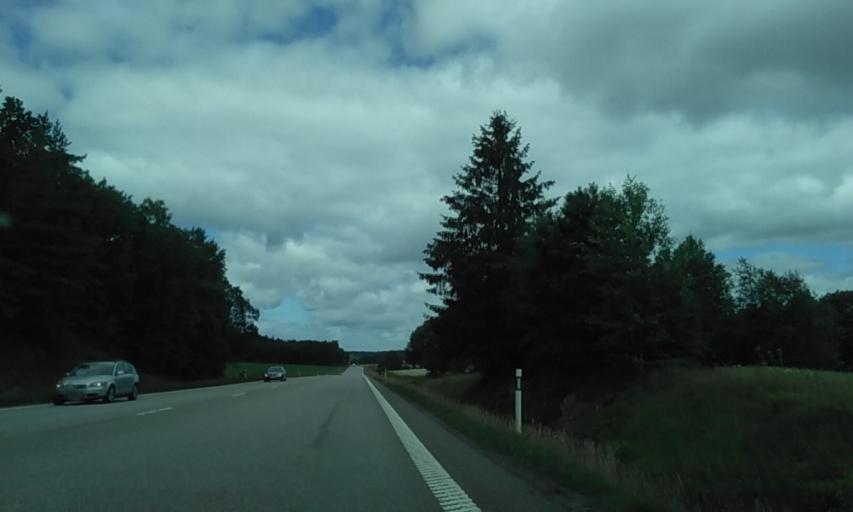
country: SE
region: Vaestra Goetaland
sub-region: Vargarda Kommun
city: Vargarda
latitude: 58.0635
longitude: 12.8181
